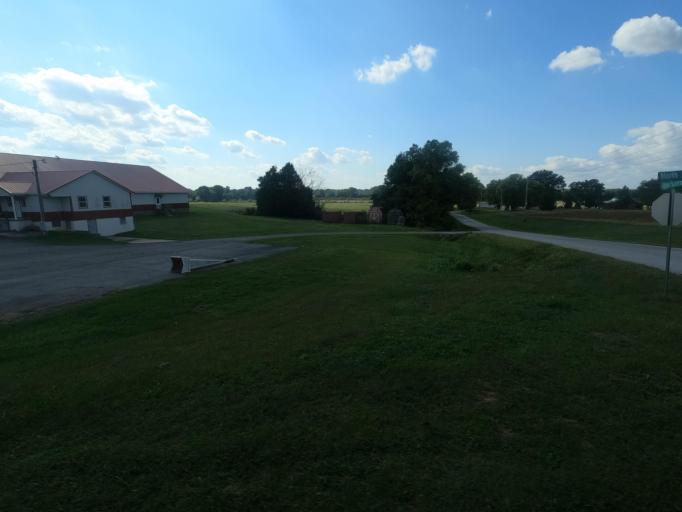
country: US
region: Illinois
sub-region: Massac County
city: Metropolis
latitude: 37.2205
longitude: -88.7292
